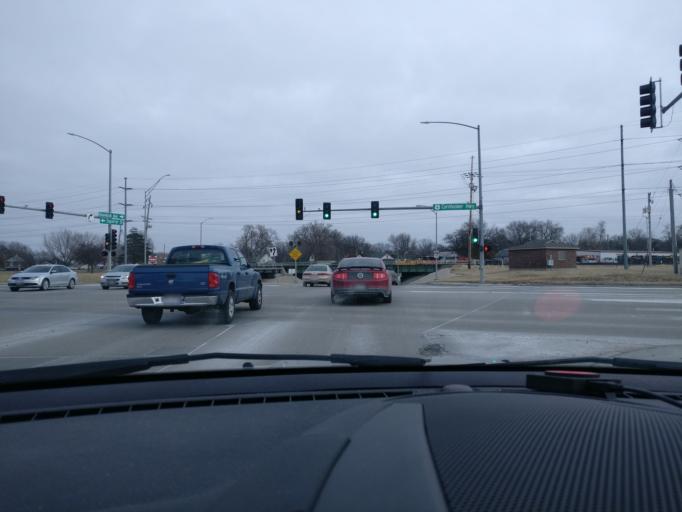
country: US
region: Nebraska
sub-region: Lancaster County
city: Lincoln
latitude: 40.8577
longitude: -96.6436
